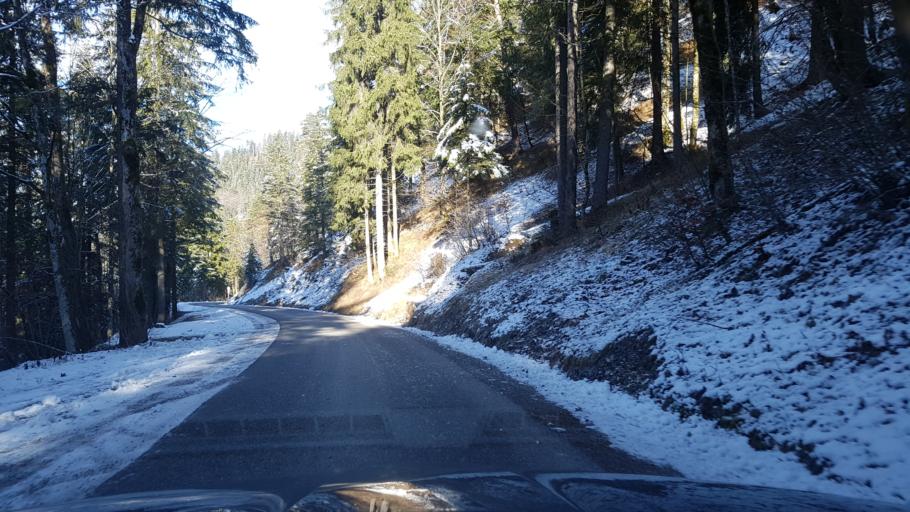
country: AT
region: Salzburg
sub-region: Politischer Bezirk Salzburg-Umgebung
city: Faistenau
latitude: 47.7638
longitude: 13.2285
